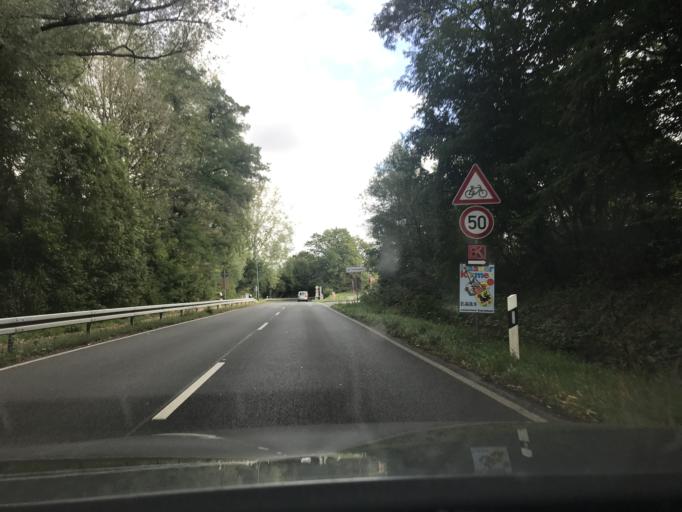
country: DE
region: North Rhine-Westphalia
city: Haan
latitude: 51.2103
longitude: 7.0020
